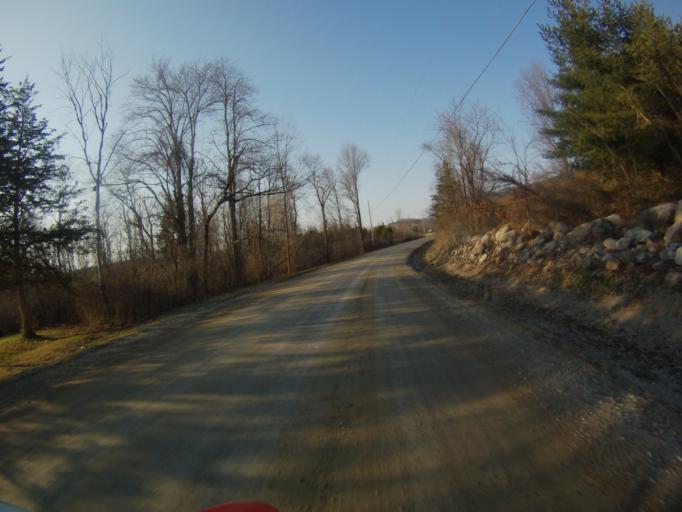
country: US
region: Vermont
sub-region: Addison County
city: Bristol
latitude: 44.1107
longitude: -73.0897
